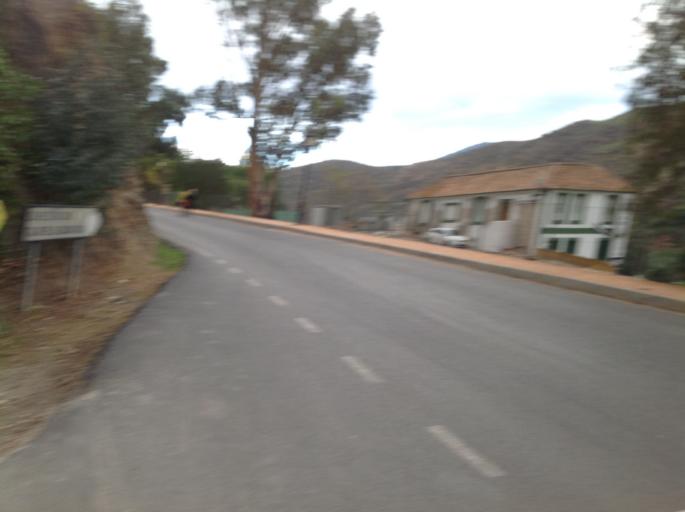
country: ES
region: Andalusia
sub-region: Provincia de Malaga
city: Carratraca
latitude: 36.9087
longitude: -4.7601
